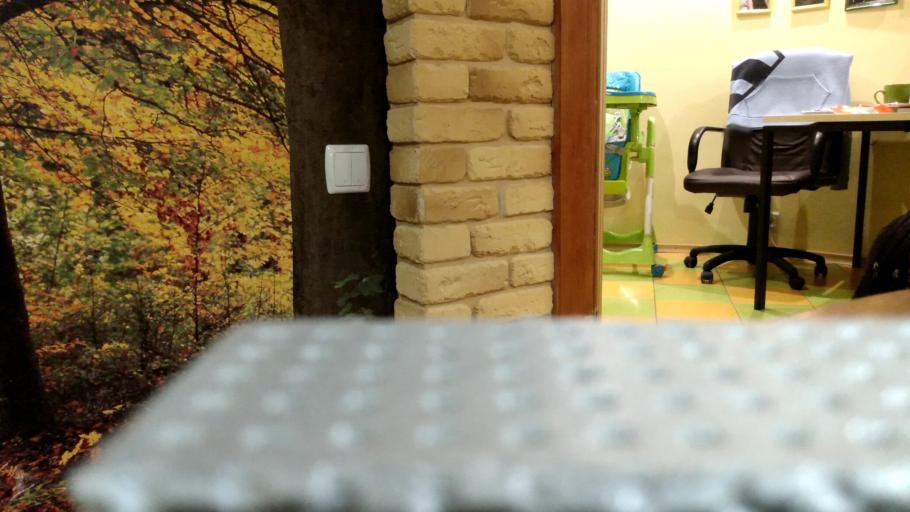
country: RU
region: Republic of Karelia
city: Pudozh
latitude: 61.9238
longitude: 37.6271
